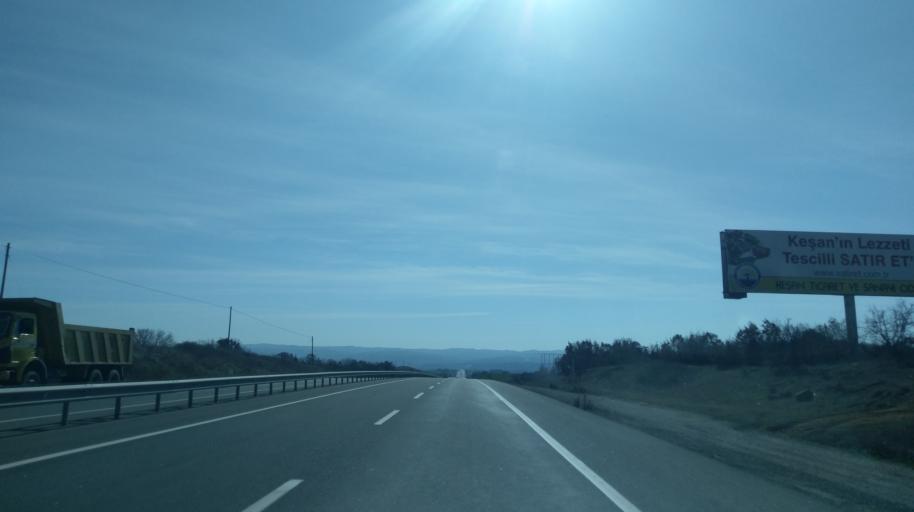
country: TR
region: Edirne
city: Kesan
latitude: 40.8039
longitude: 26.6626
